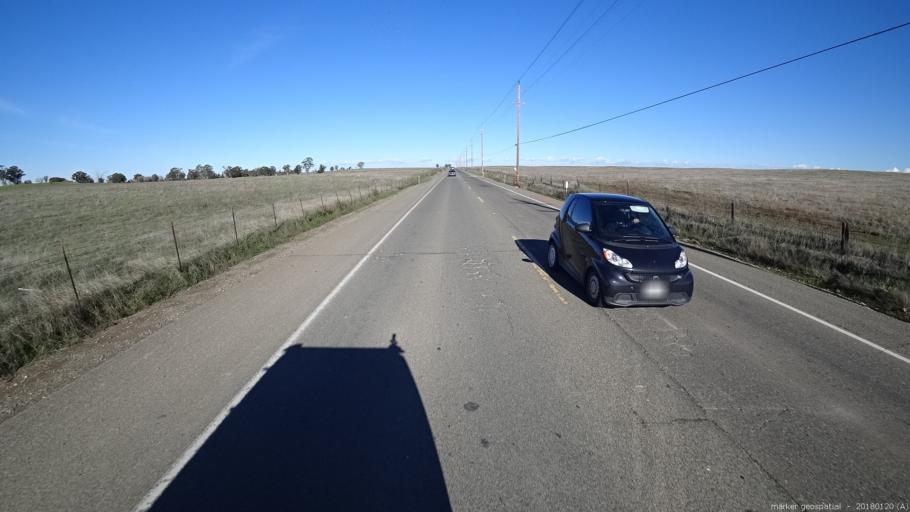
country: US
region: California
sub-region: Sacramento County
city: Rancho Murieta
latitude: 38.5129
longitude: -121.2112
